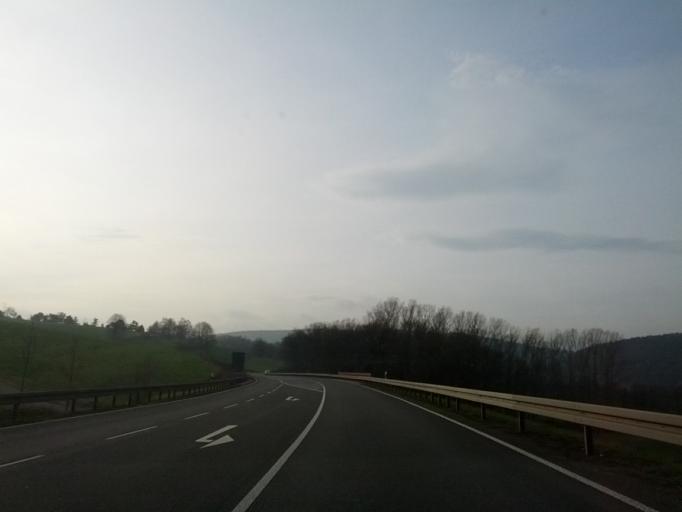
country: DE
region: Thuringia
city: Schwallungen
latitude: 50.6867
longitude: 10.3585
